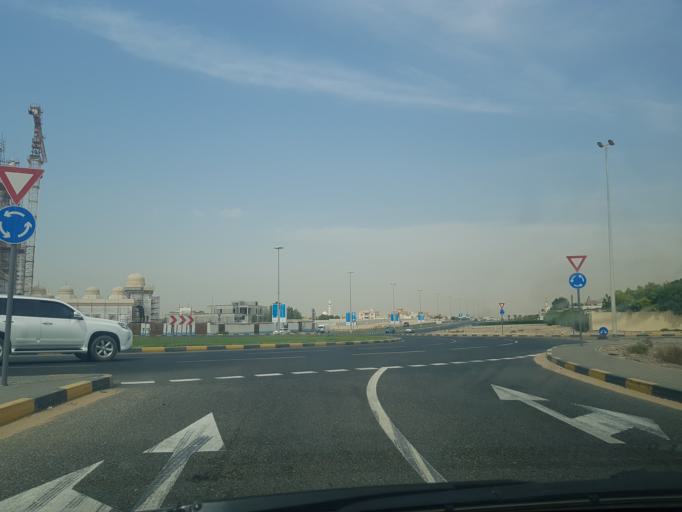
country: AE
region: Ash Shariqah
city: Sharjah
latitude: 25.2710
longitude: 55.4859
